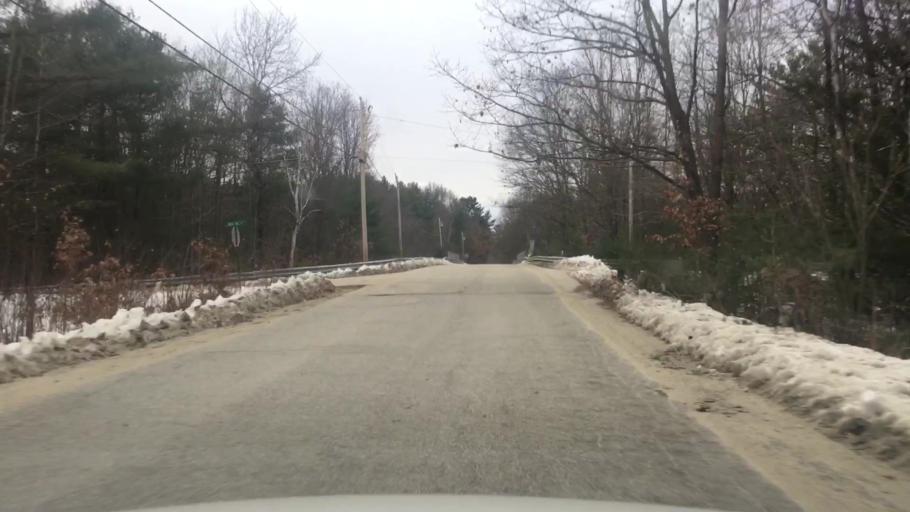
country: US
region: New Hampshire
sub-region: Merrimack County
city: Hopkinton
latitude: 43.1819
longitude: -71.6747
